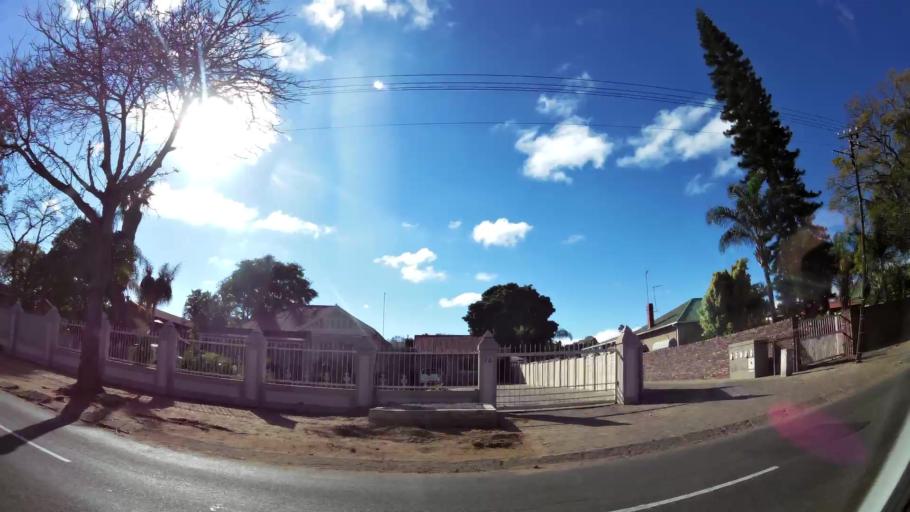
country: ZA
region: Limpopo
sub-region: Capricorn District Municipality
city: Polokwane
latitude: -23.9047
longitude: 29.4589
